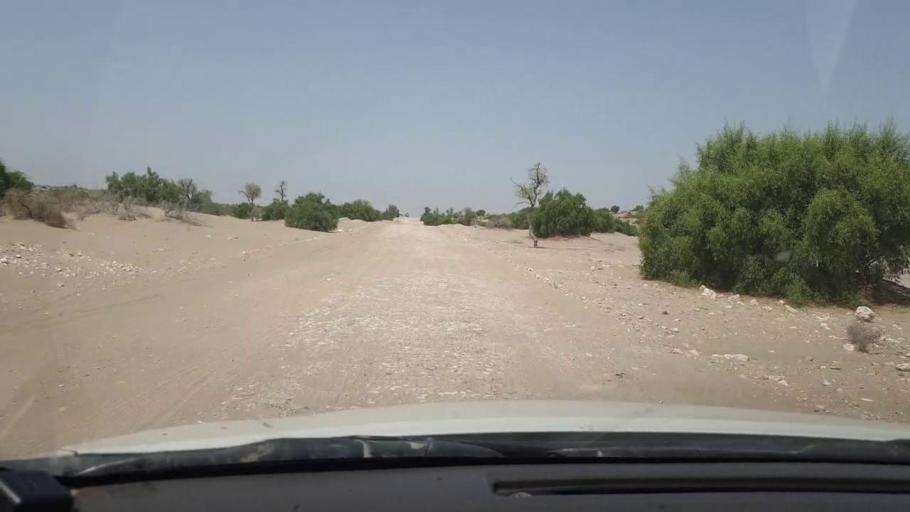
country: PK
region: Sindh
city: Rohri
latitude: 27.2911
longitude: 69.2579
